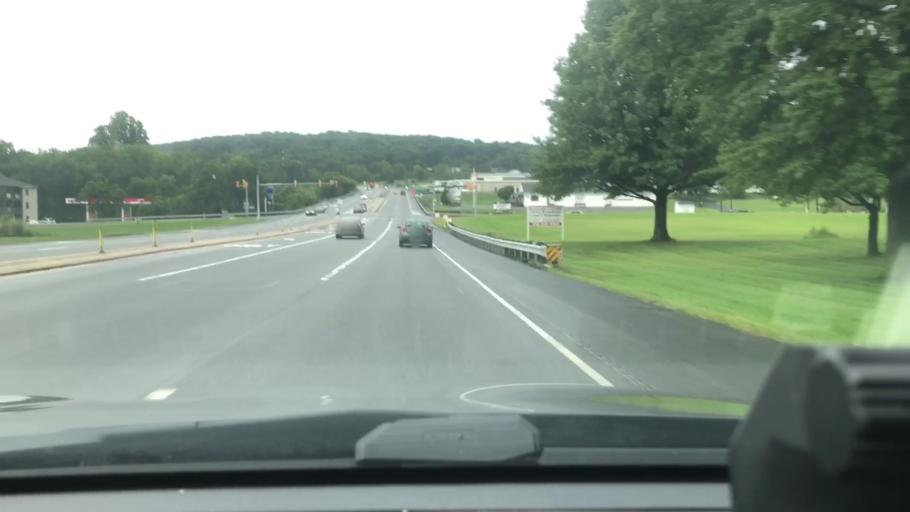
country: US
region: Pennsylvania
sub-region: Berks County
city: Boyertown
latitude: 40.3116
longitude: -75.6331
